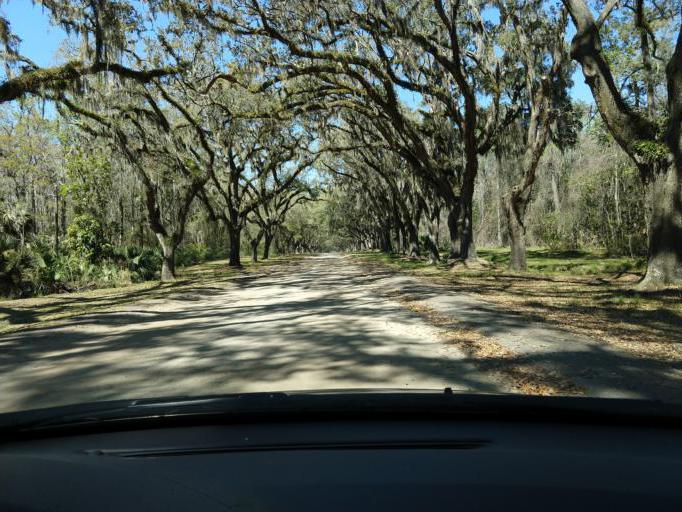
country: US
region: Georgia
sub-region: Chatham County
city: Isle of Hope
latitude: 31.9721
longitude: -81.0692
